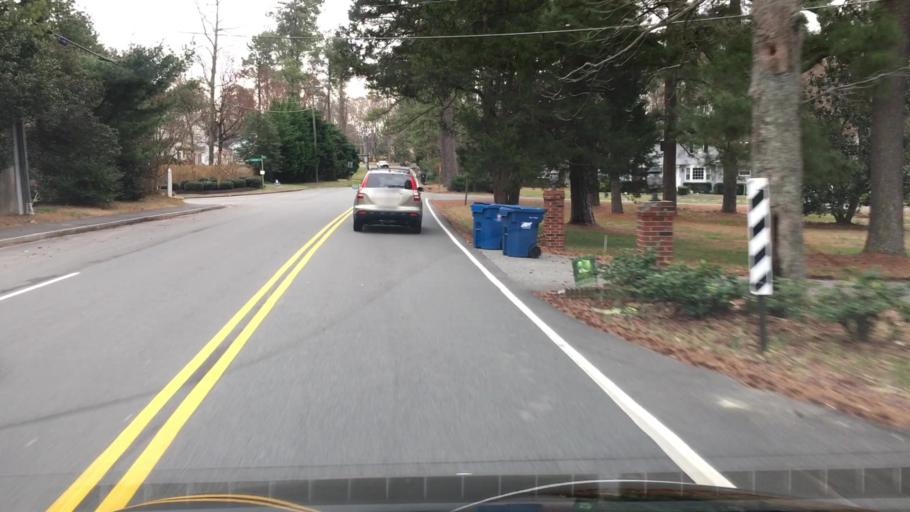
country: US
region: Virginia
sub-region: Henrico County
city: Tuckahoe
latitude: 37.5897
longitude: -77.5931
